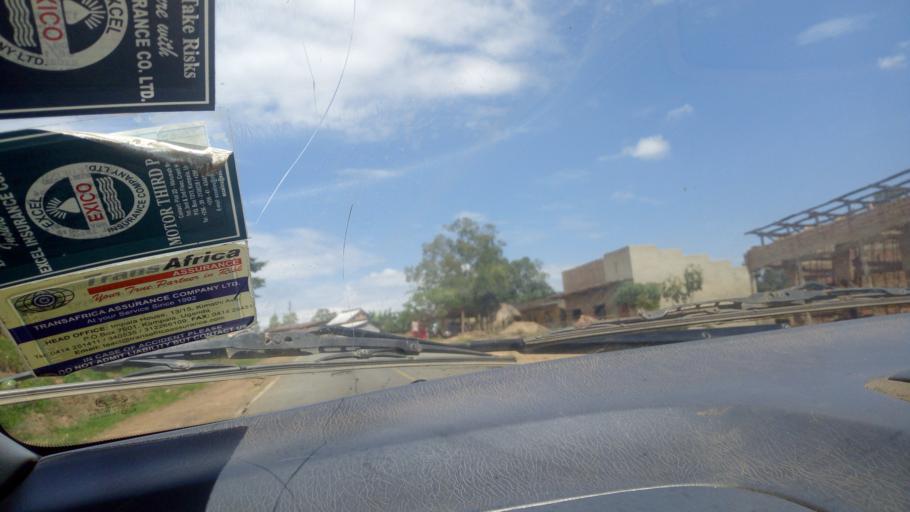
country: UG
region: Western Region
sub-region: Buhweju District
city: Buhweju
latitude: -0.2743
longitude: 30.5639
